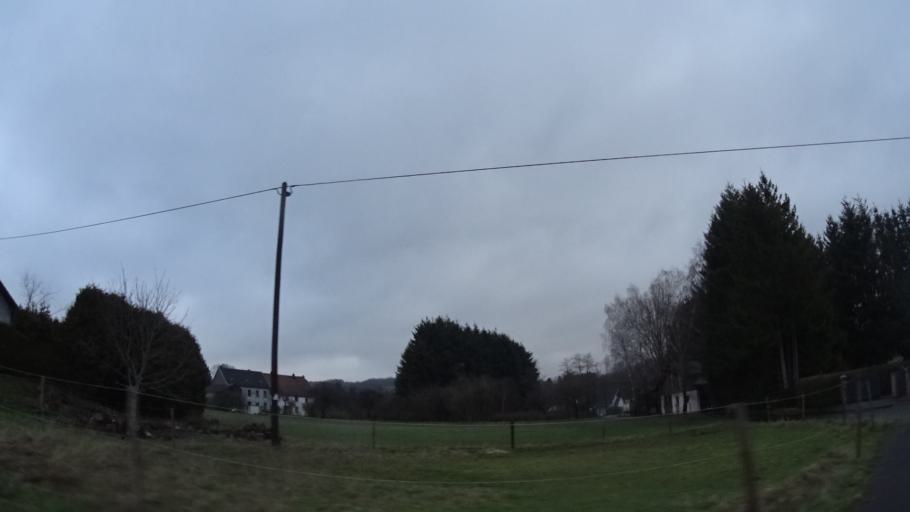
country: DE
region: Rheinland-Pfalz
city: Brucken
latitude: 49.6338
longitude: 7.1126
